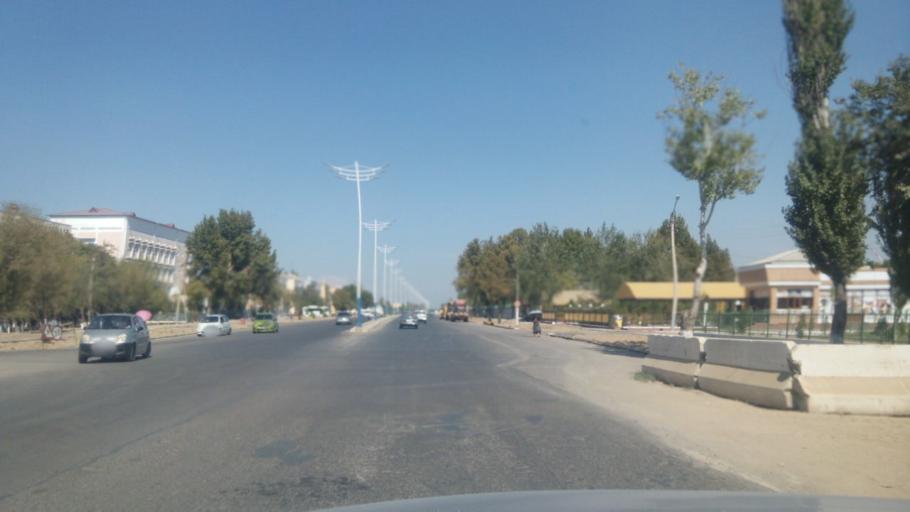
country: UZ
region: Sirdaryo
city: Guliston
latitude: 40.5120
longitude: 68.7792
